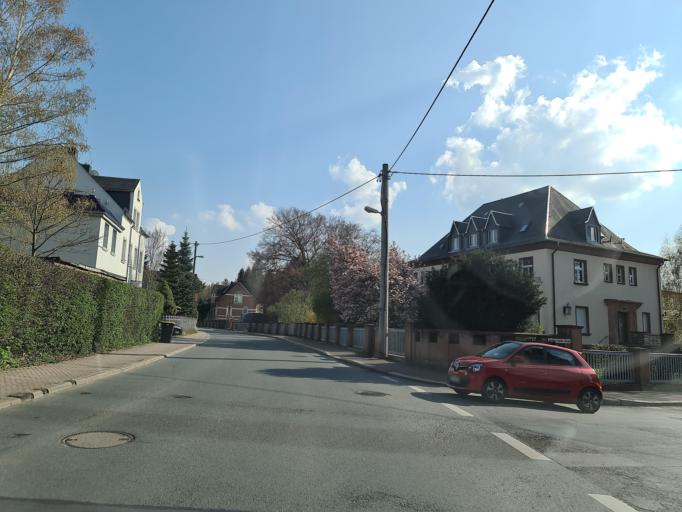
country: DE
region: Saxony
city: Neukirchen
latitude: 50.7604
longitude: 12.8753
